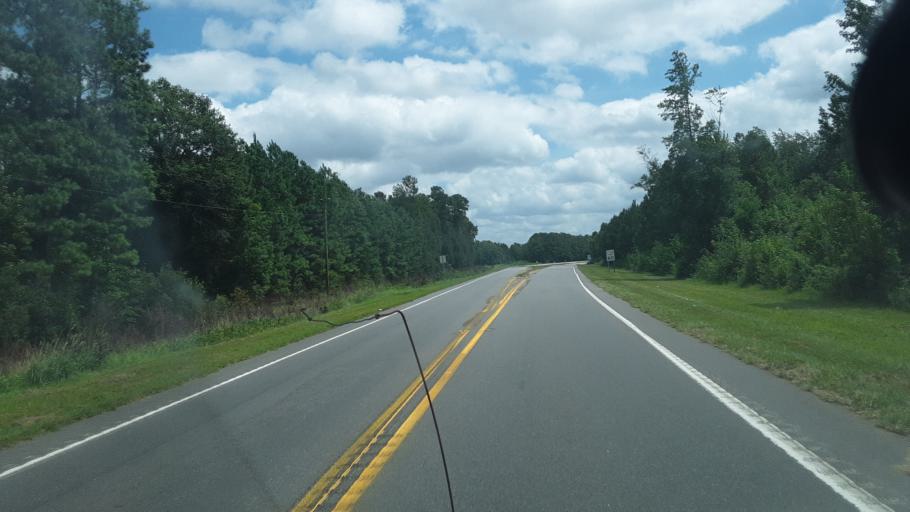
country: US
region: North Carolina
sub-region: Columbus County
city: Tabor City
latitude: 34.1320
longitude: -78.9925
